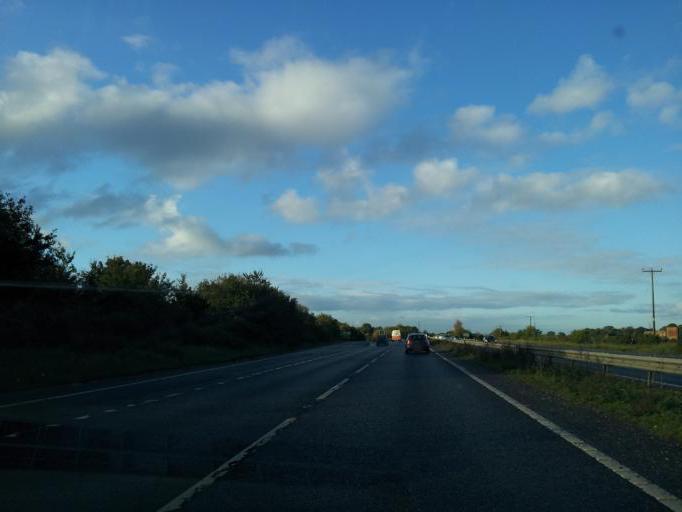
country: GB
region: England
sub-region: Norfolk
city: Cringleford
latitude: 52.5903
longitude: 1.2814
